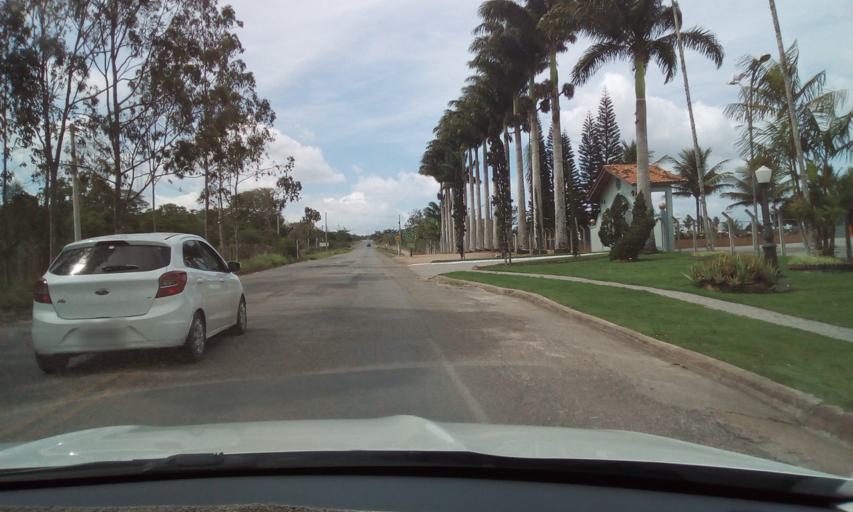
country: BR
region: Pernambuco
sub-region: Bezerros
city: Bezerros
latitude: -8.2830
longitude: -35.7423
